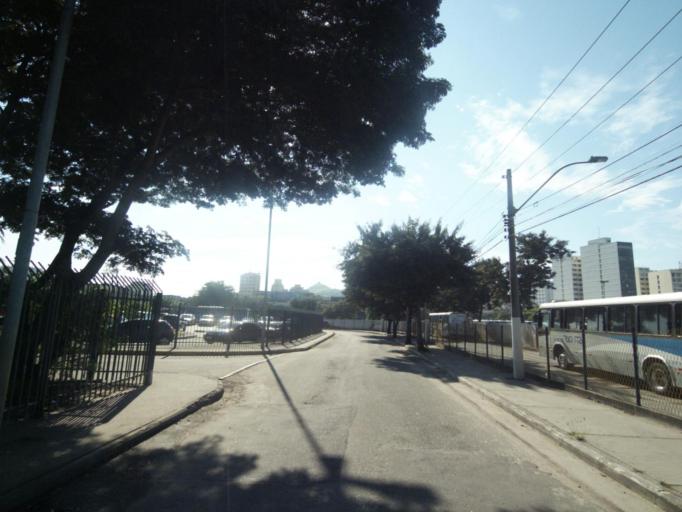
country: BR
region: Rio de Janeiro
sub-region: Niteroi
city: Niteroi
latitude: -22.8896
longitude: -43.1258
